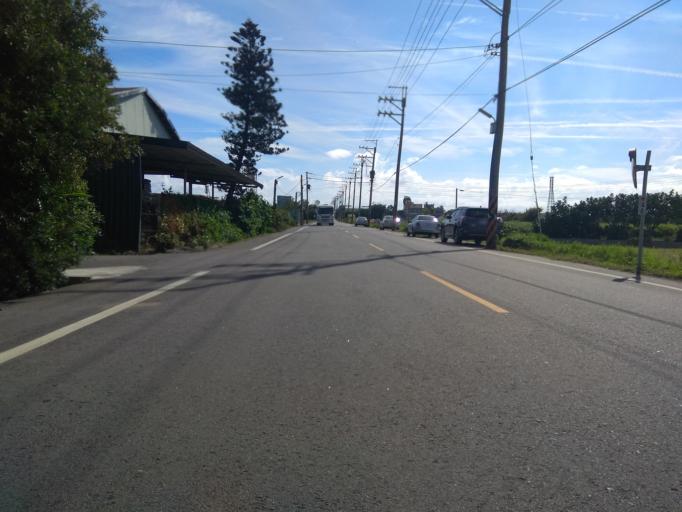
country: TW
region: Taiwan
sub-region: Hsinchu
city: Zhubei
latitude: 25.0110
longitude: 121.0389
